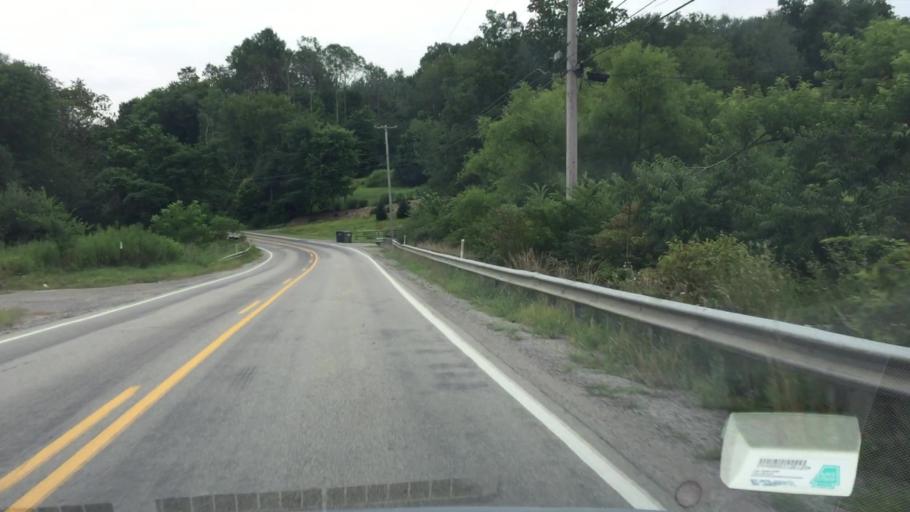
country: US
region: Pennsylvania
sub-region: Allegheny County
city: Curtisville
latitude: 40.6915
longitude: -79.8385
